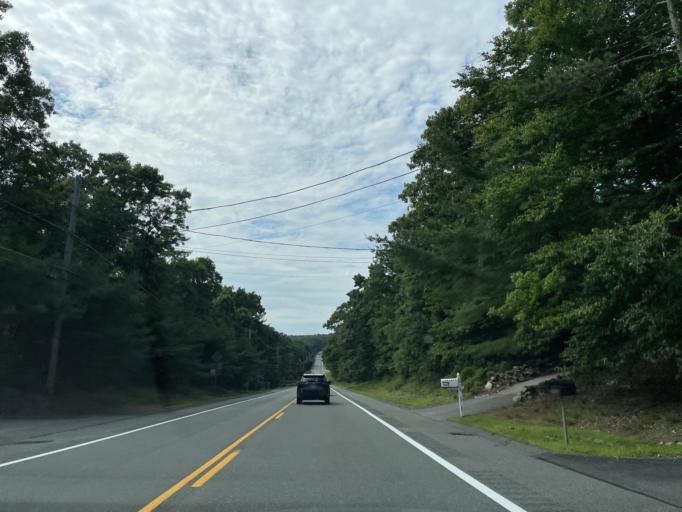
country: US
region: Rhode Island
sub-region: Kent County
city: West Greenwich
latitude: 41.6219
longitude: -71.6757
